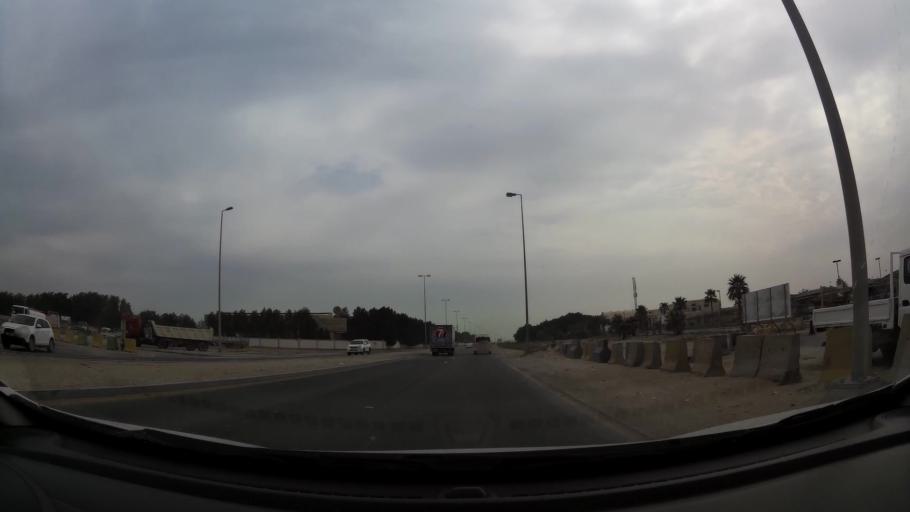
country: BH
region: Northern
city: Sitrah
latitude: 26.0854
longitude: 50.6119
